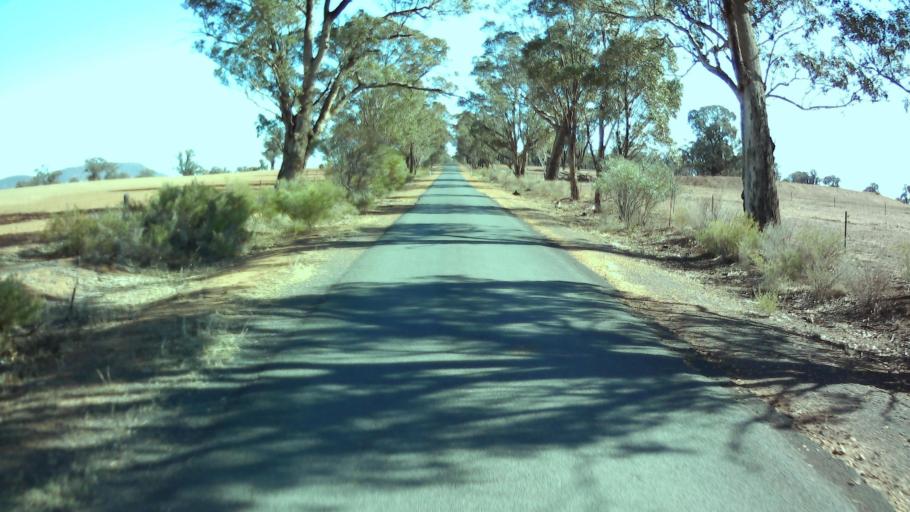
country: AU
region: New South Wales
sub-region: Weddin
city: Grenfell
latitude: -33.7904
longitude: 147.9576
